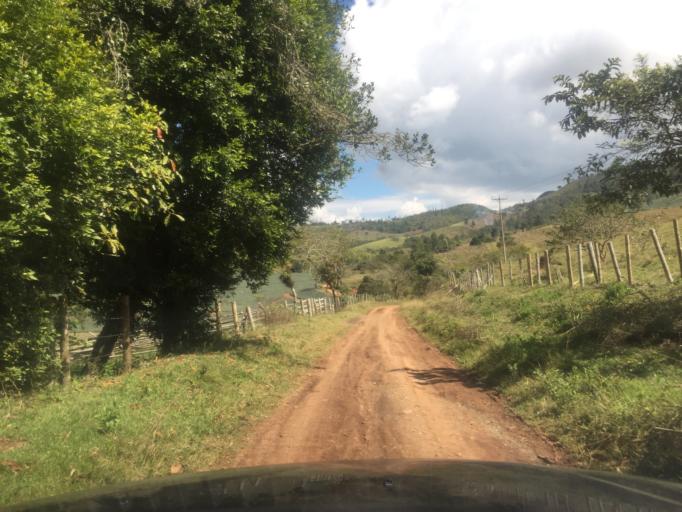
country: CO
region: Valle del Cauca
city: Yumbo
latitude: 3.6594
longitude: -76.5479
